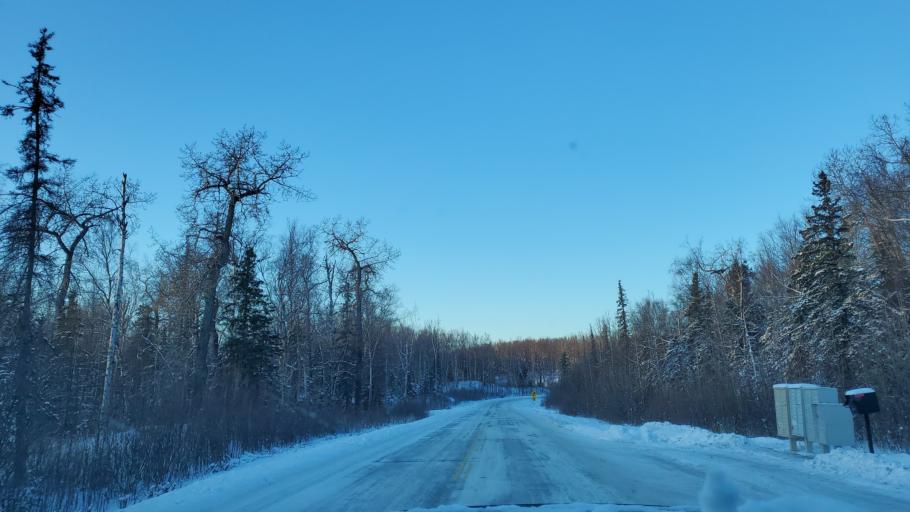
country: US
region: Alaska
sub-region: Matanuska-Susitna Borough
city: Lakes
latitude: 61.6356
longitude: -149.3005
